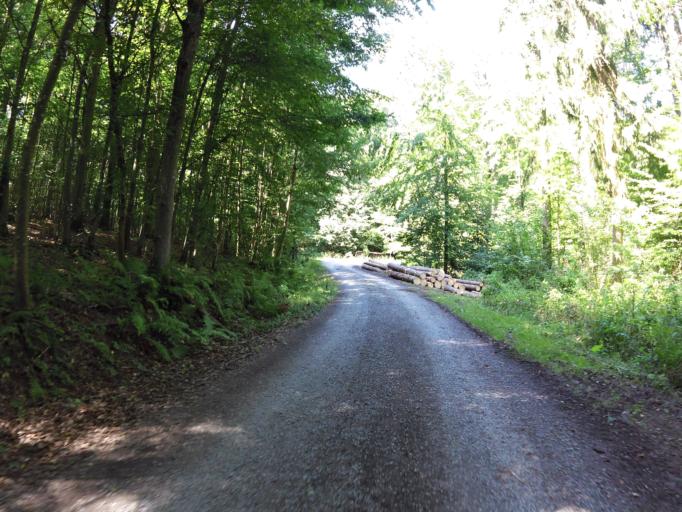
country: DE
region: Bavaria
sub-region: Regierungsbezirk Unterfranken
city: Guntersleben
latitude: 49.8596
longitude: 9.8803
